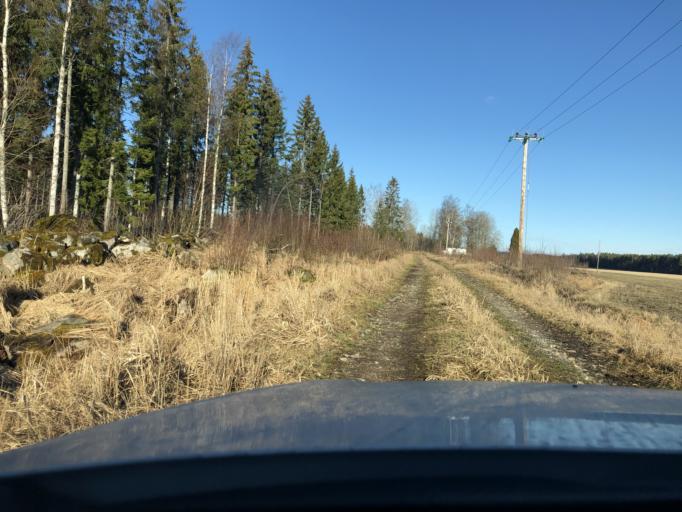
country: SE
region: Gaevleborg
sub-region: Gavle Kommun
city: Hedesunda
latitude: 60.3050
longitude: 16.9007
